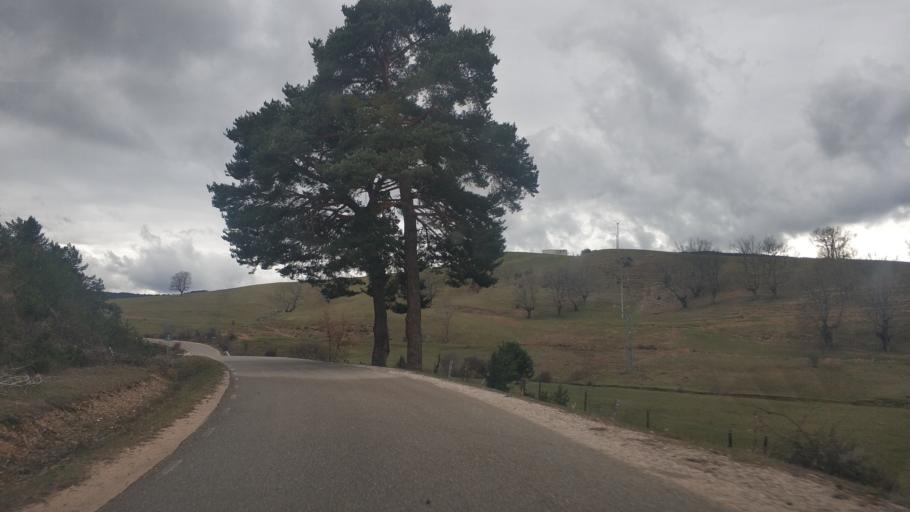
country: ES
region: Castille and Leon
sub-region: Provincia de Burgos
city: Canicosa de la Sierra
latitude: 41.9447
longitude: -3.0359
